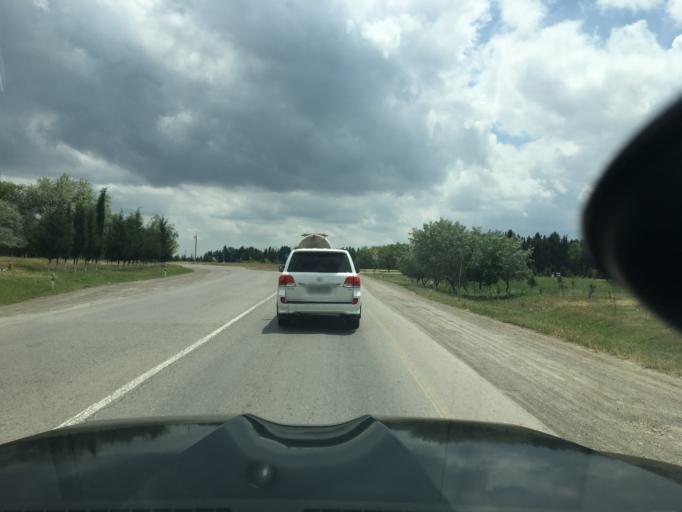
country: AZ
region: Tovuz
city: Qaraxanli
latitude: 41.0302
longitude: 45.5975
